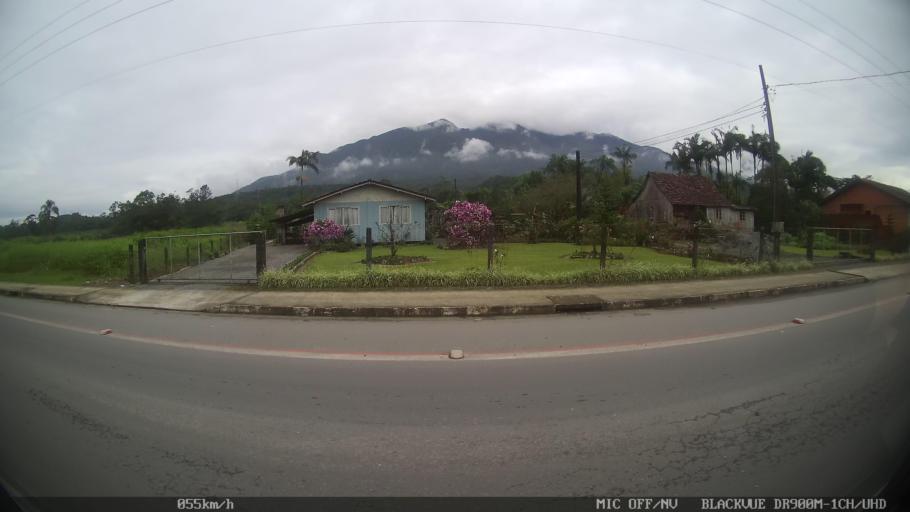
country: BR
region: Santa Catarina
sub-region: Joinville
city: Joinville
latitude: -26.0563
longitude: -48.8570
